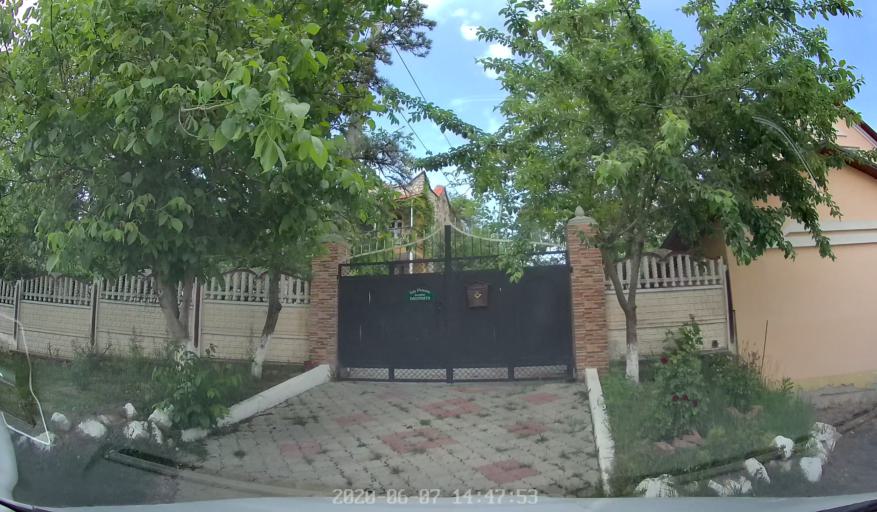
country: MD
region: Laloveni
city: Ialoveni
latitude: 46.9818
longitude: 28.7057
